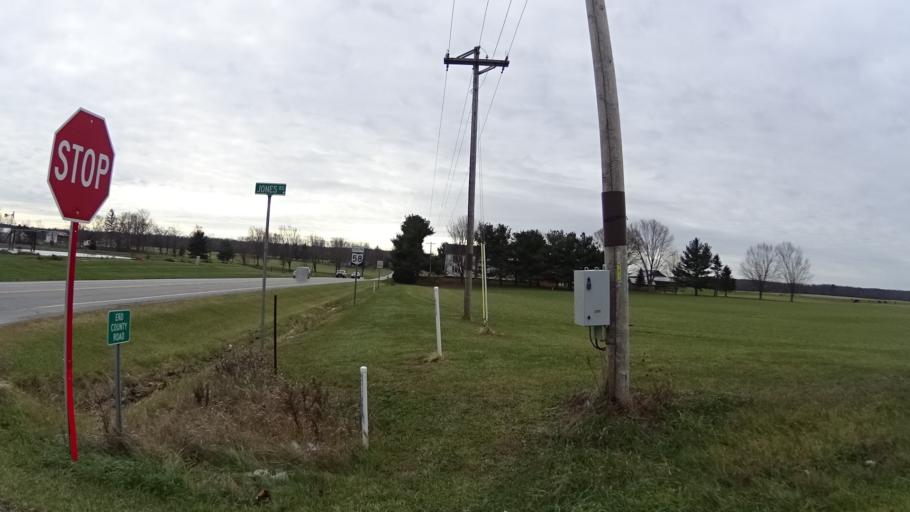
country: US
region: Ohio
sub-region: Lorain County
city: Wellington
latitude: 41.1479
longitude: -82.2182
